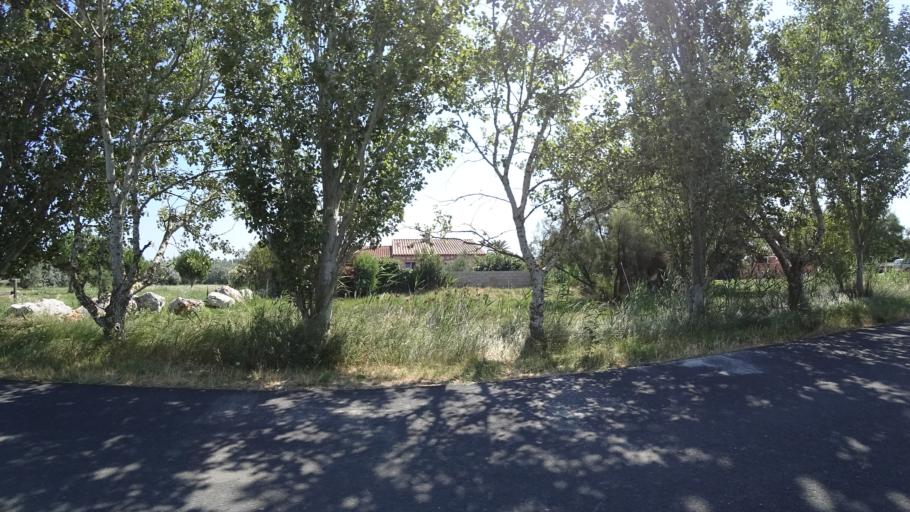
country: FR
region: Languedoc-Roussillon
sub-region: Departement des Pyrenees-Orientales
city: Sainte-Marie-Plage
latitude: 42.7353
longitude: 3.0255
